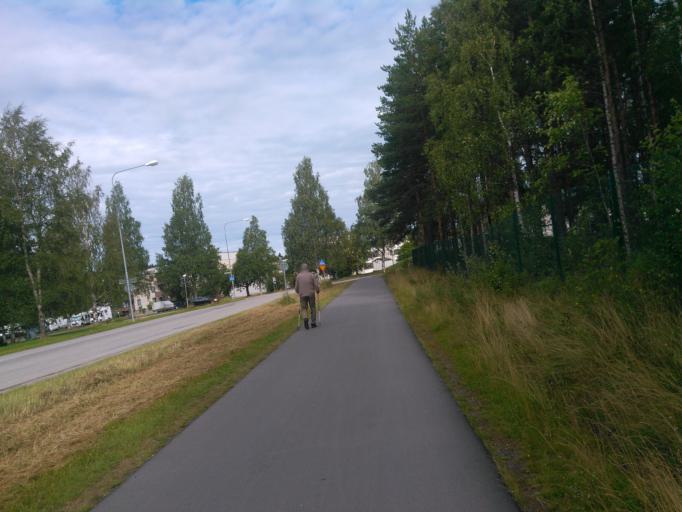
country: SE
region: Vaesterbotten
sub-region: Umea Kommun
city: Ersmark
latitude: 63.8310
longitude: 20.3230
